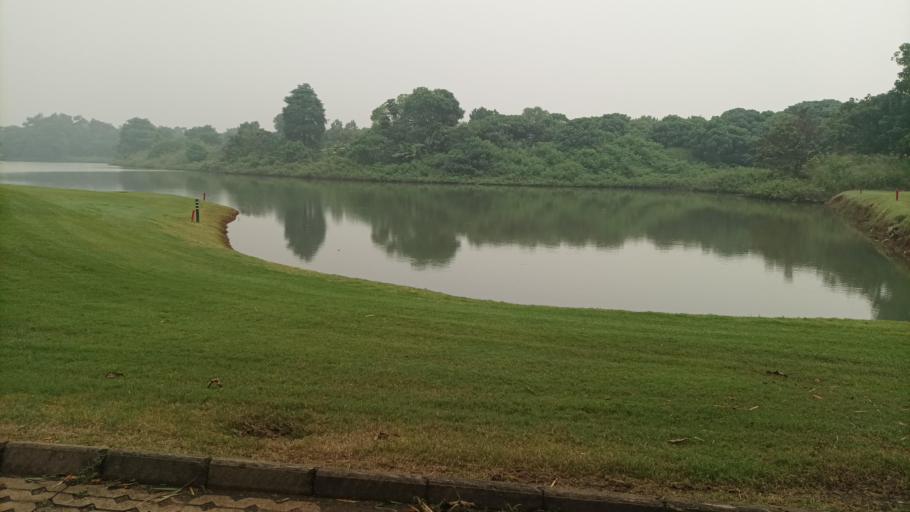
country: ID
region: West Java
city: Cileungsir
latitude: -6.4171
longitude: 106.8967
